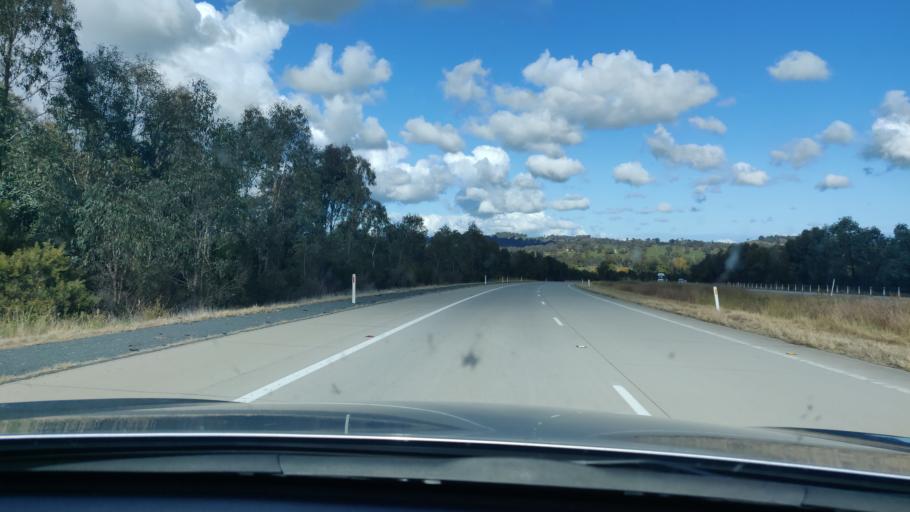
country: AU
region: New South Wales
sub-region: Greater Hume Shire
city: Holbrook
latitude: -35.8172
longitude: 147.2390
